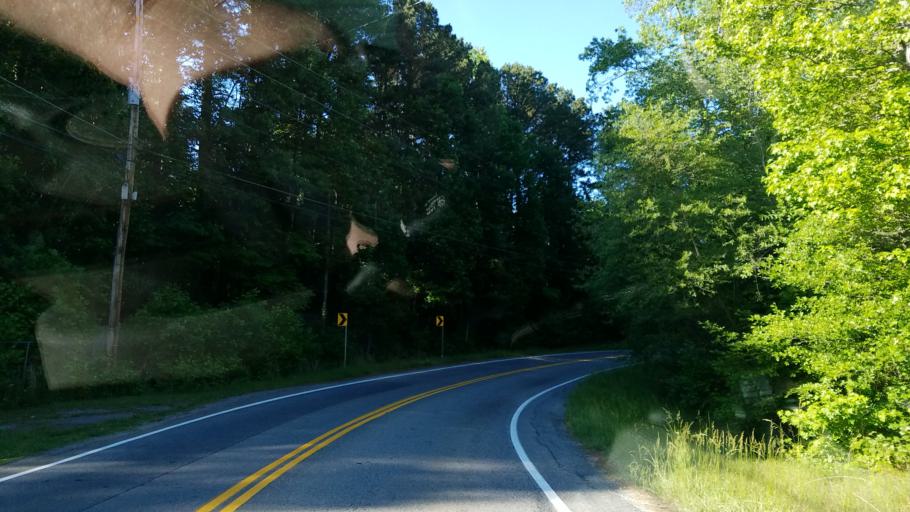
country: US
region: Georgia
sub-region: Cherokee County
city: Woodstock
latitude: 34.1512
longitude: -84.5883
